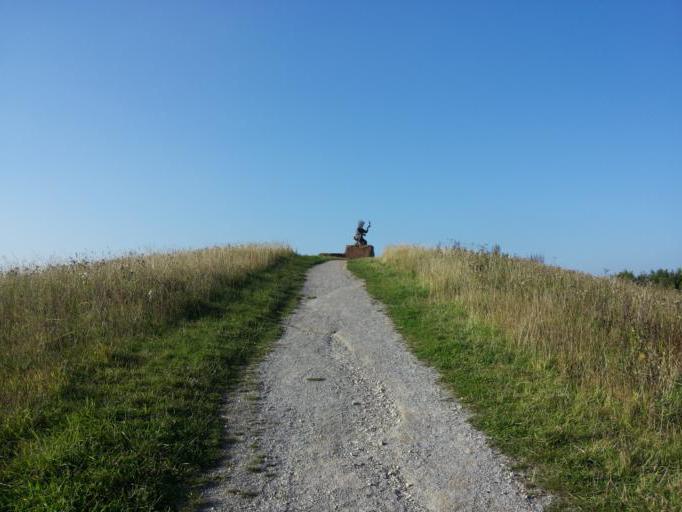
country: GB
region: England
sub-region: Derbyshire
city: Tibshelf
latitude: 53.1539
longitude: -1.2973
